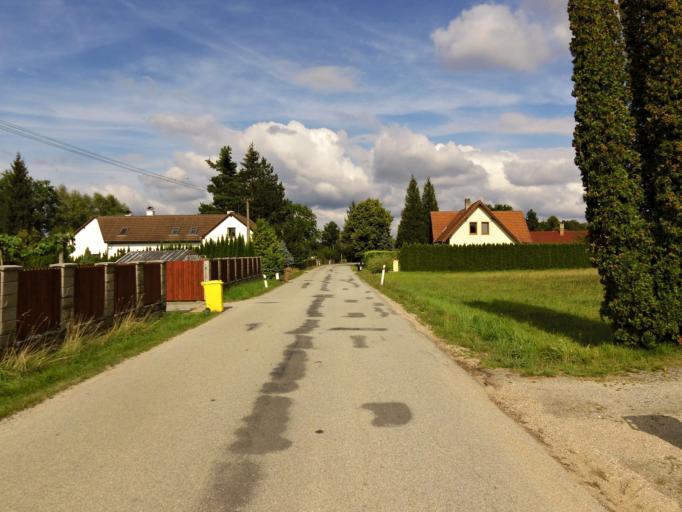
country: CZ
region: Jihocesky
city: Suchdol nad Luznici
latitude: 48.8895
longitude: 14.8445
